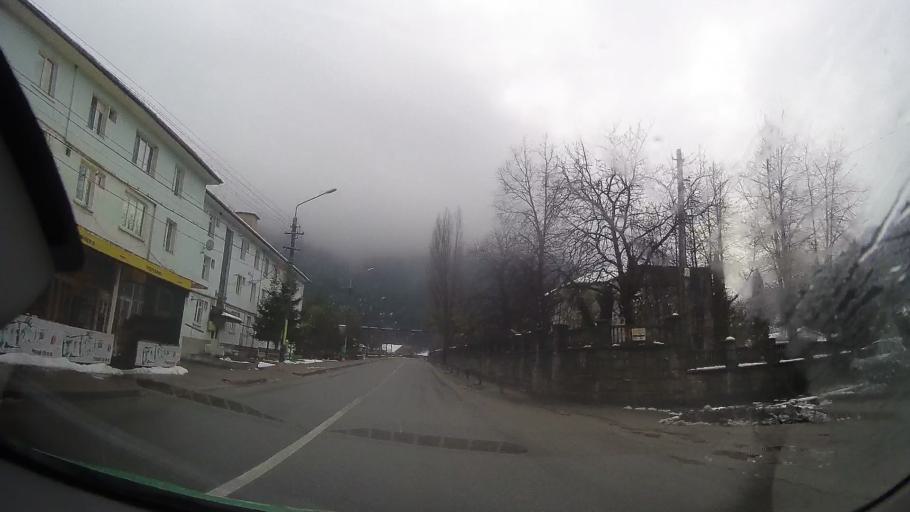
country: RO
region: Neamt
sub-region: Comuna Bicaz
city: Bicaz
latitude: 46.9028
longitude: 26.0740
